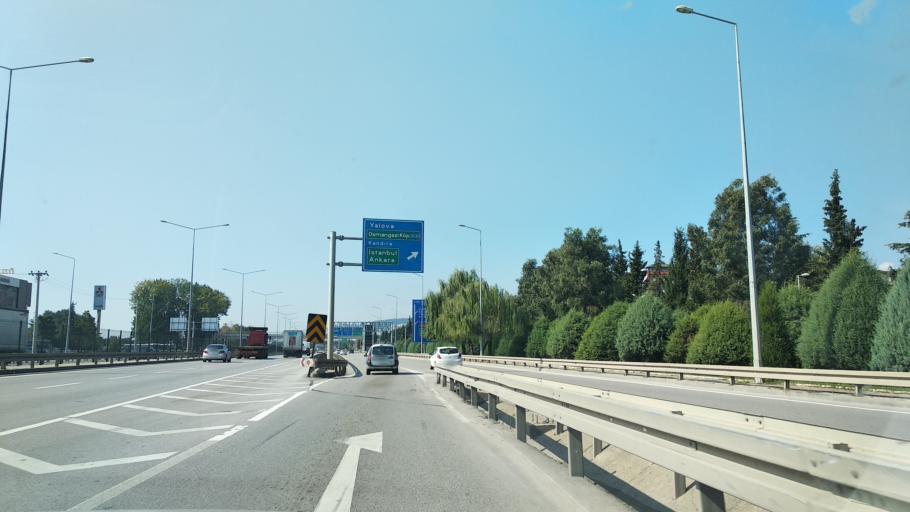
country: TR
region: Kocaeli
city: Kullar
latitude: 40.7608
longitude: 29.9737
